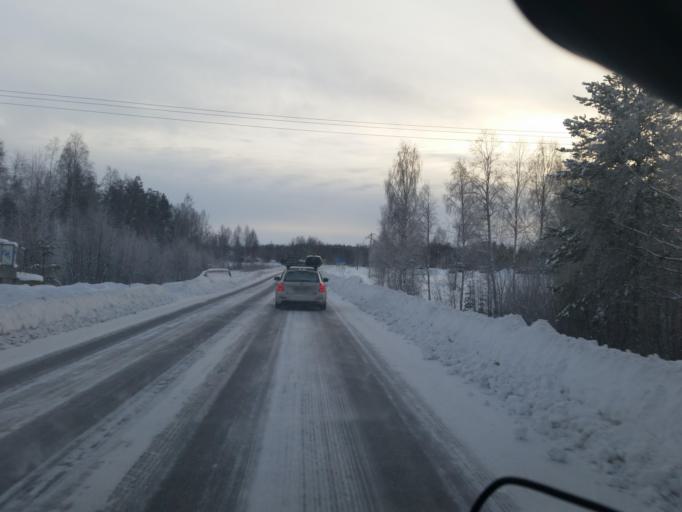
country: SE
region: Norrbotten
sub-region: Pitea Kommun
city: Norrfjarden
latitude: 65.4254
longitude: 21.4949
